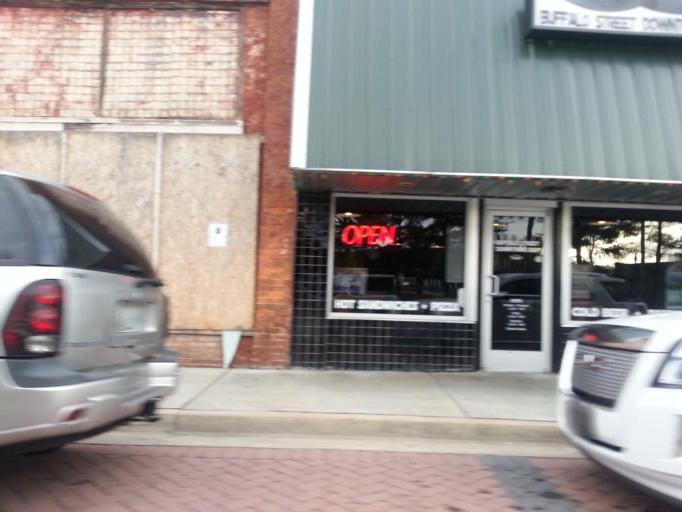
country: US
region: Tennessee
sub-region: Washington County
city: Johnson City
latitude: 36.3159
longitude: -82.3530
